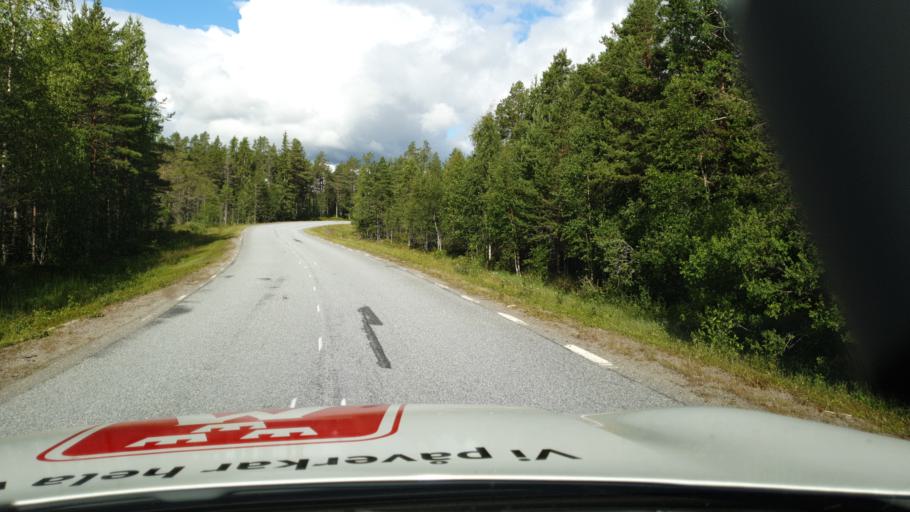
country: SE
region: Vaesterbotten
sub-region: Umea Kommun
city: Roback
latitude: 63.6749
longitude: 20.0962
